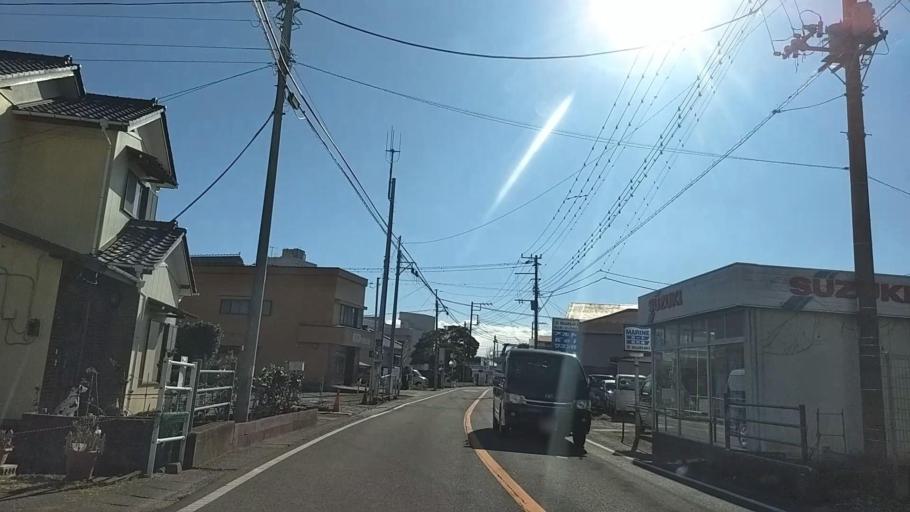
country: JP
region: Chiba
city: Tateyama
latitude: 34.9848
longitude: 139.8615
